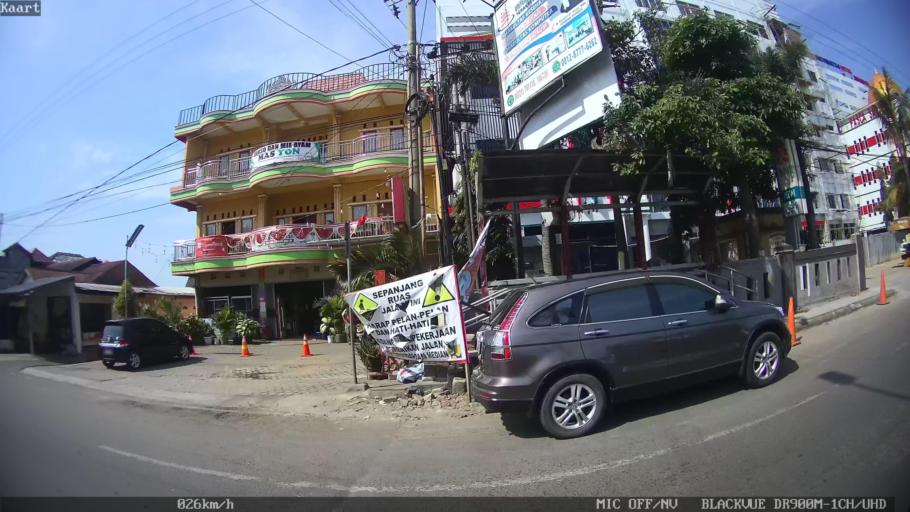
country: ID
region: Lampung
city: Kedaton
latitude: -5.3732
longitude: 105.2422
